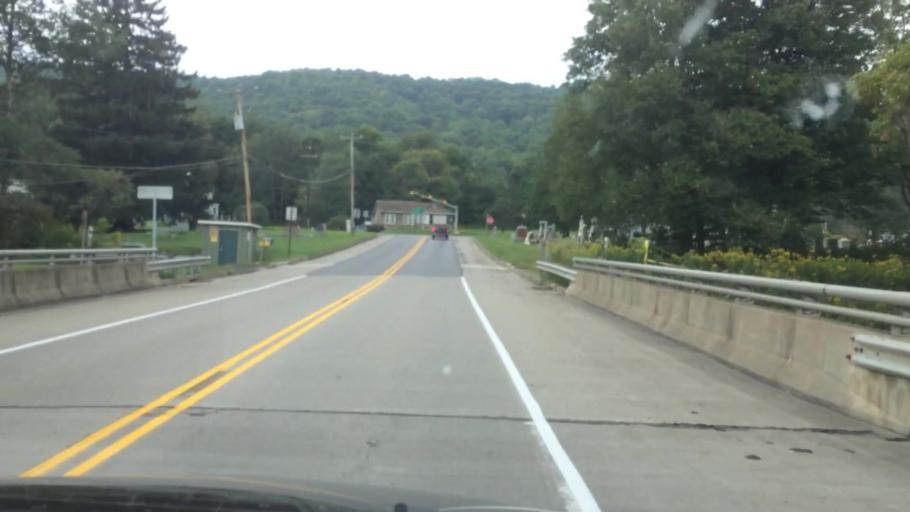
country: US
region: Pennsylvania
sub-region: McKean County
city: Bradford
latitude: 41.9145
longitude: -78.6496
